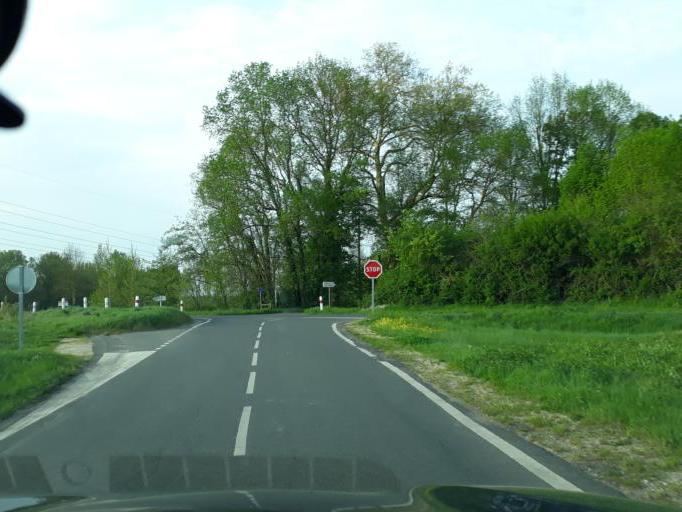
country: FR
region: Centre
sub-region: Departement du Loiret
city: Tavers
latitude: 47.7394
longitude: 1.6423
